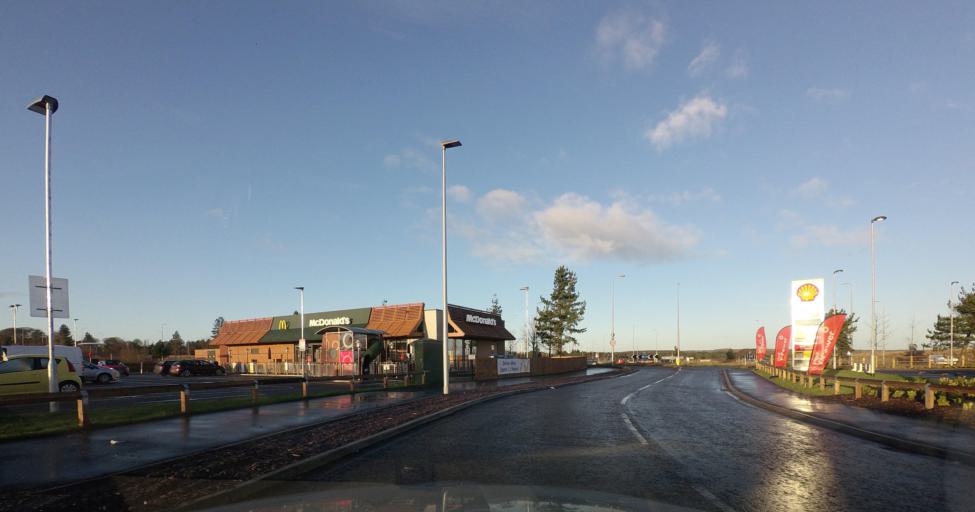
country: GB
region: Scotland
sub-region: West Lothian
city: Armadale
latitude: 55.8681
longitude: -3.7037
